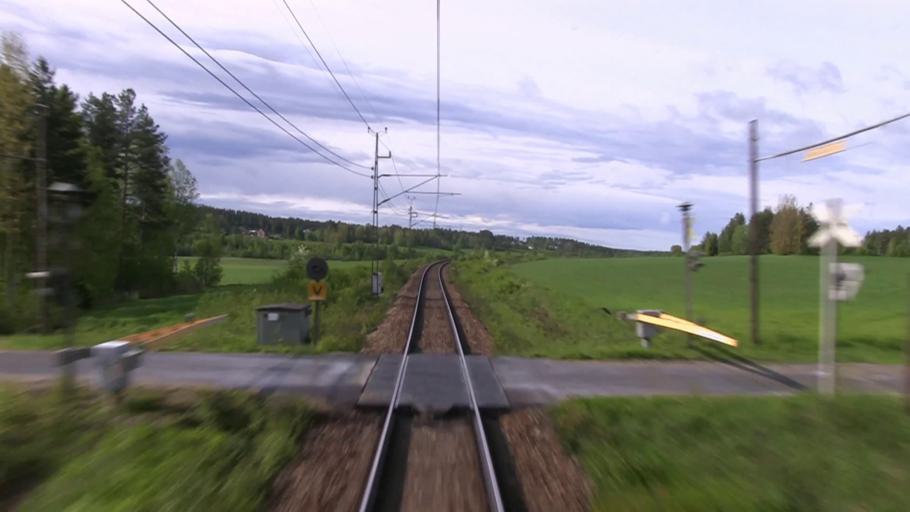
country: SE
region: Vaesterbotten
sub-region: Vindelns Kommun
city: Vindeln
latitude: 64.1071
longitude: 19.6848
